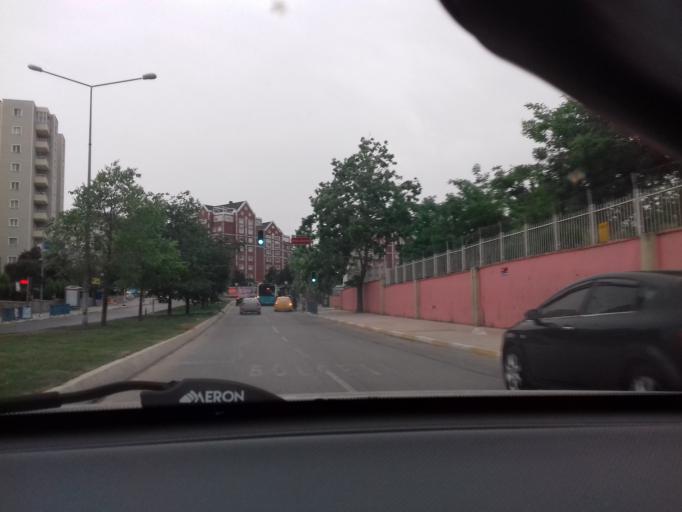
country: TR
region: Istanbul
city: Sultanbeyli
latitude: 40.9291
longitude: 29.2970
